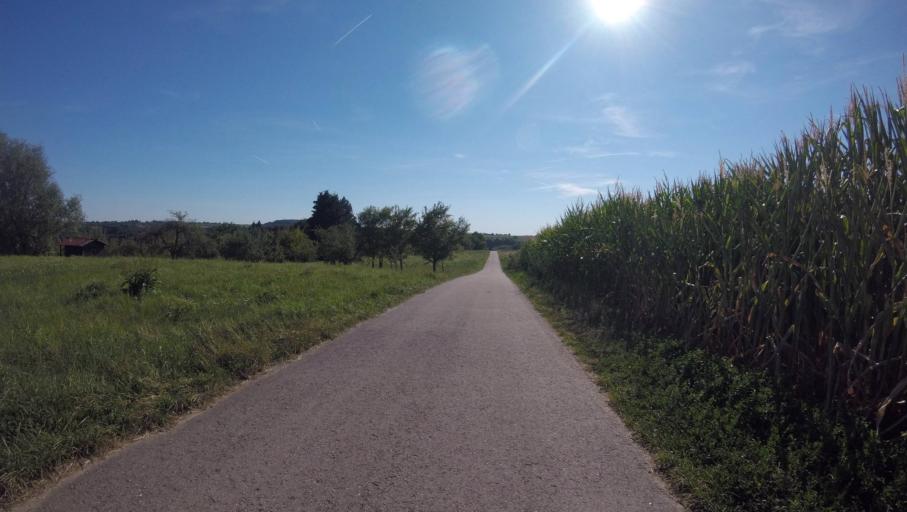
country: DE
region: Baden-Wuerttemberg
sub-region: Regierungsbezirk Stuttgart
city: Kirchberg an der Murr
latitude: 48.9469
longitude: 9.3313
